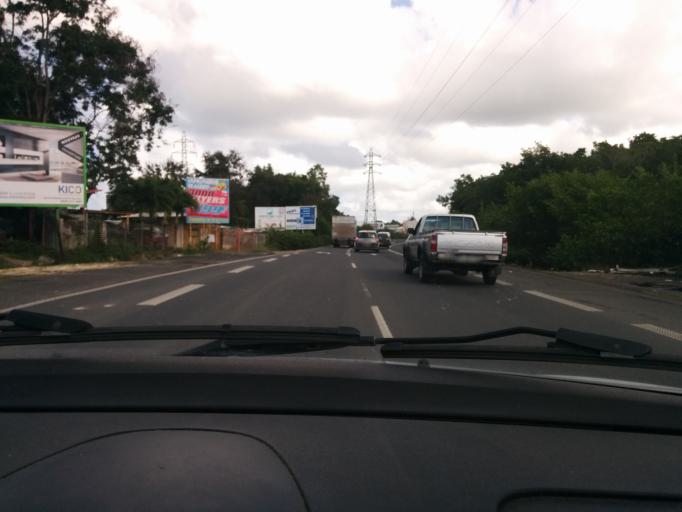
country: GP
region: Guadeloupe
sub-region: Guadeloupe
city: Pointe-a-Pitre
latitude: 16.2493
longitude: -61.5543
